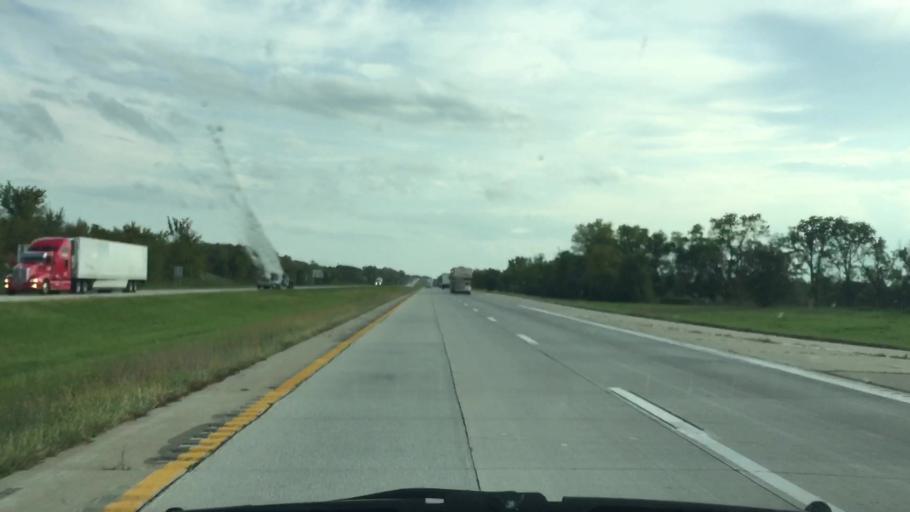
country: US
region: Missouri
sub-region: Daviess County
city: Gallatin
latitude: 39.9941
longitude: -94.0957
